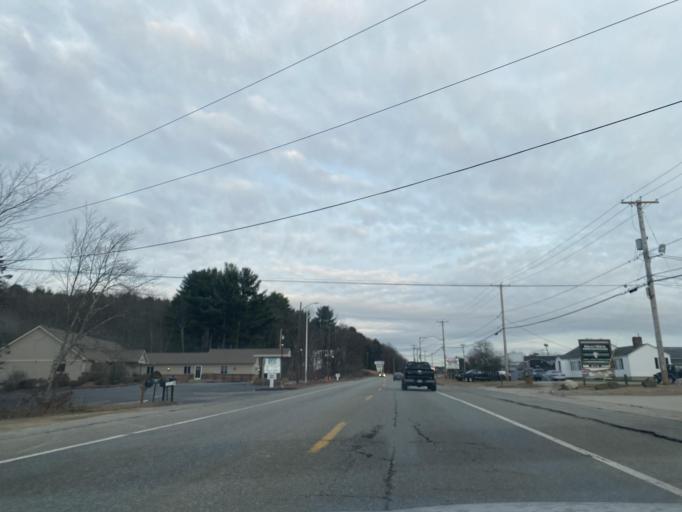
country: US
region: Massachusetts
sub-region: Worcester County
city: East Brookfield
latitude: 42.2316
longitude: -72.0263
